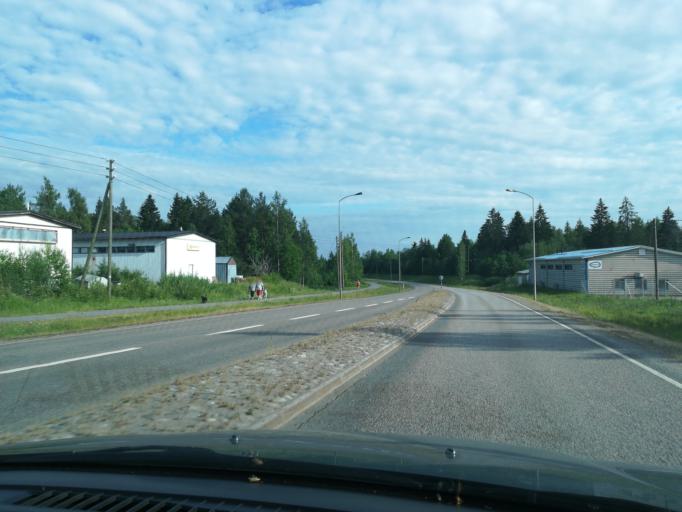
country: FI
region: South Karelia
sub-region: Imatra
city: Imatra
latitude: 61.1617
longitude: 28.7897
